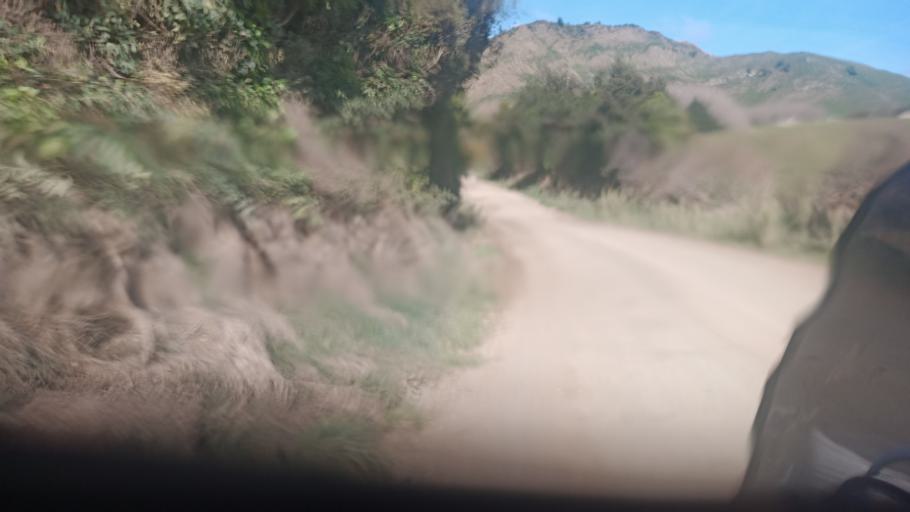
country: NZ
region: Gisborne
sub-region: Gisborne District
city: Gisborne
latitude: -38.4292
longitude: 177.5615
